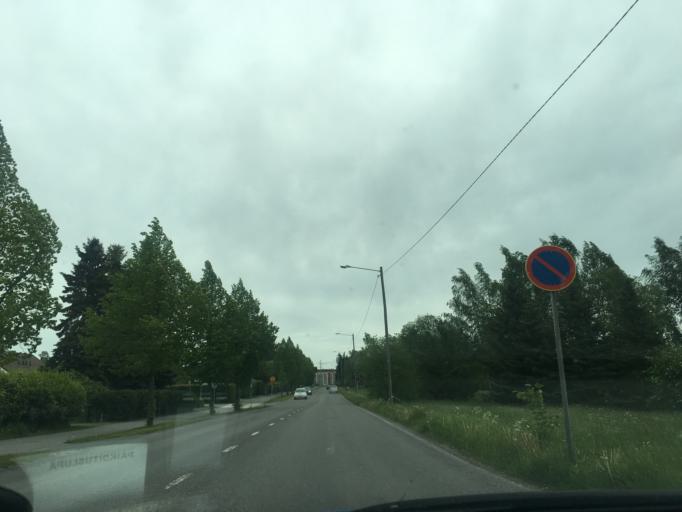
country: FI
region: Varsinais-Suomi
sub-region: Turku
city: Turku
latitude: 60.4727
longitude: 22.2991
